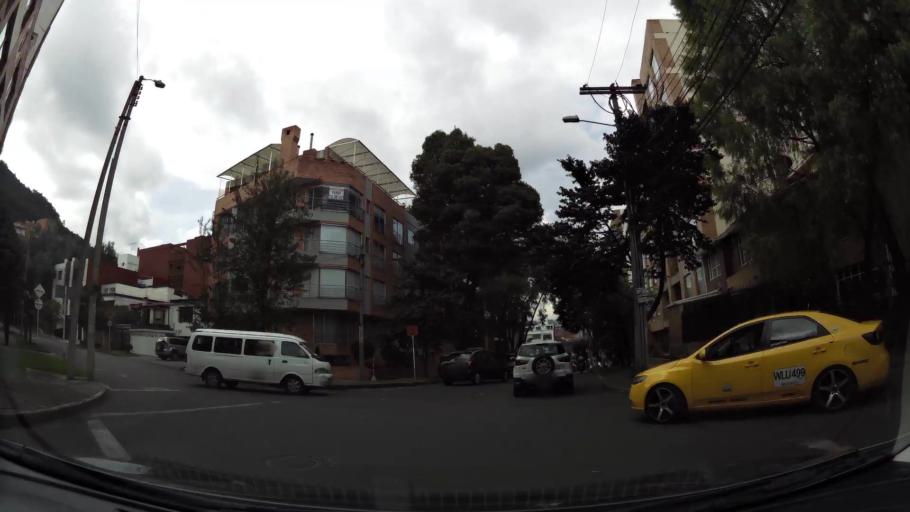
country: CO
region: Bogota D.C.
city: Barrio San Luis
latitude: 4.7040
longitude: -74.0308
